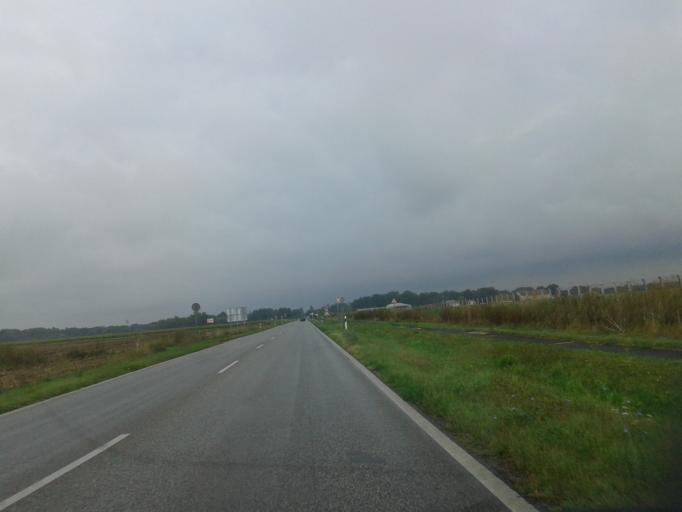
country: HU
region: Csongrad
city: Szeged
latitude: 46.2526
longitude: 20.0874
